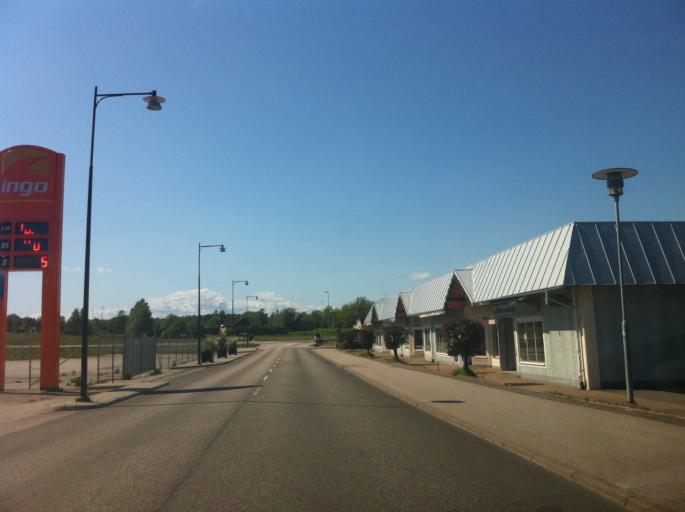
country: SE
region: Vaestra Goetaland
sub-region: Gullspangs Kommun
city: Gullspang
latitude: 58.9866
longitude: 14.0931
